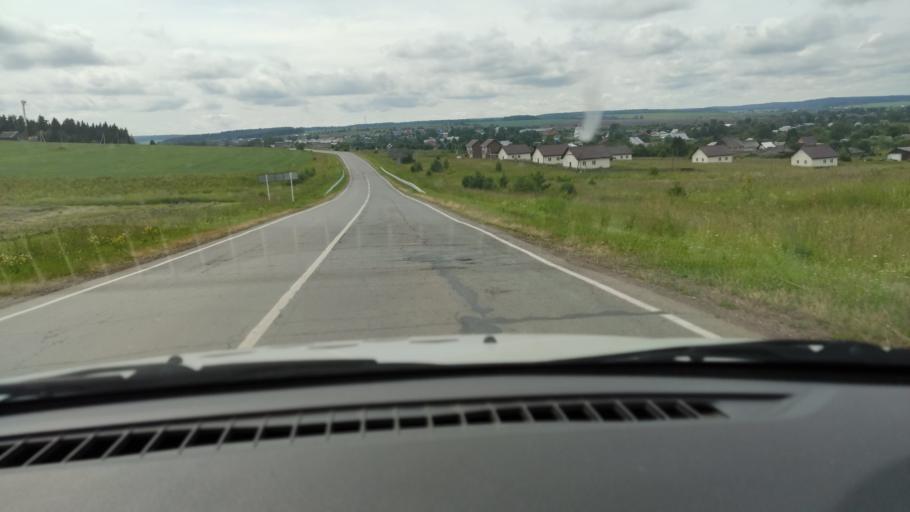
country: RU
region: Perm
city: Kukushtan
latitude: 57.4671
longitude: 56.5523
